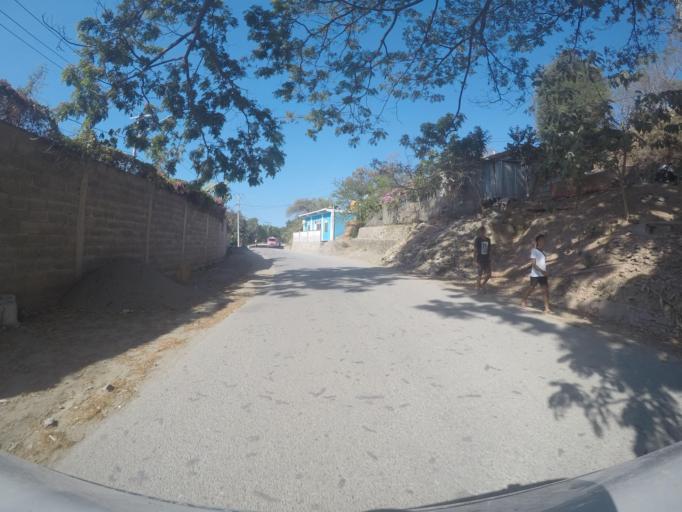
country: TL
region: Dili
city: Dili
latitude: -8.5751
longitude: 125.5377
